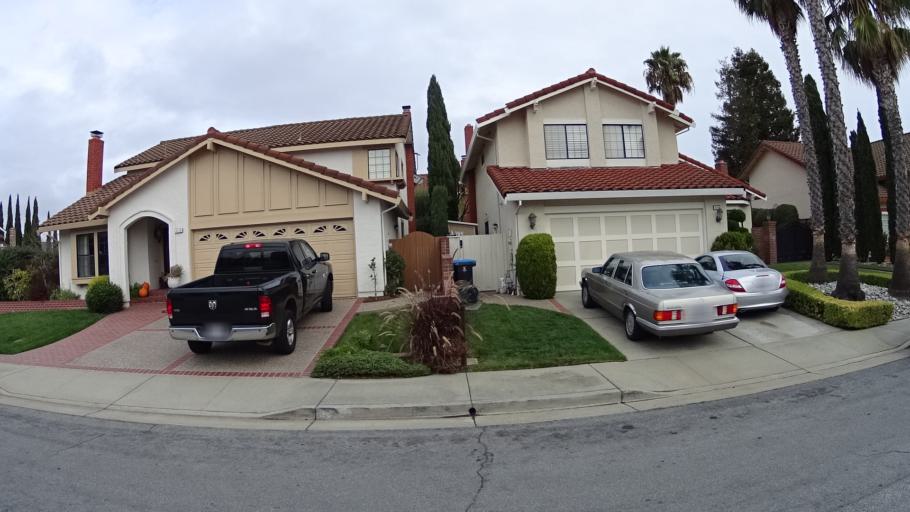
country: US
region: California
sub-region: San Mateo County
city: Belmont
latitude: 37.5295
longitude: -122.2797
